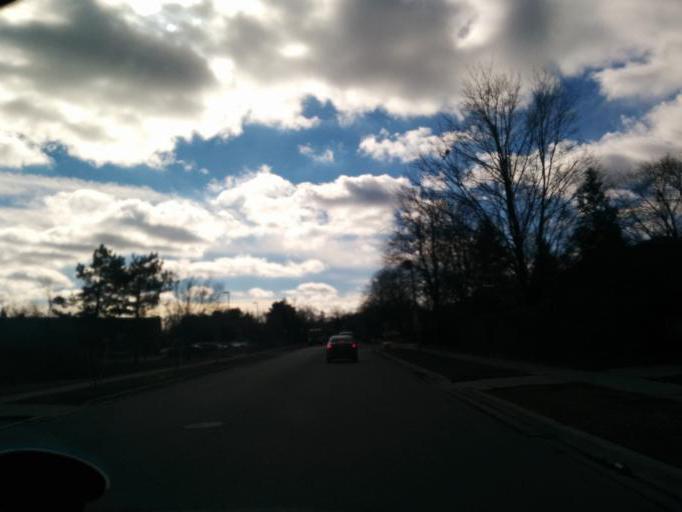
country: CA
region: Ontario
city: Mississauga
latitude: 43.5374
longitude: -79.6771
